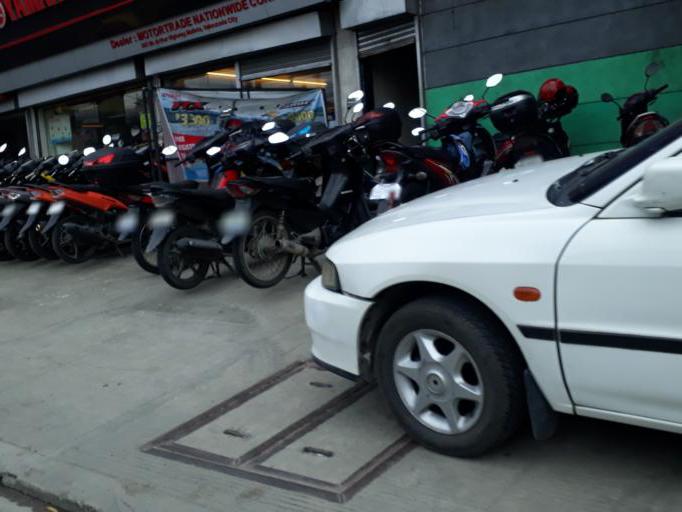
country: PH
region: Calabarzon
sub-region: Province of Rizal
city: Valenzuela
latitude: 14.6943
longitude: 120.9641
